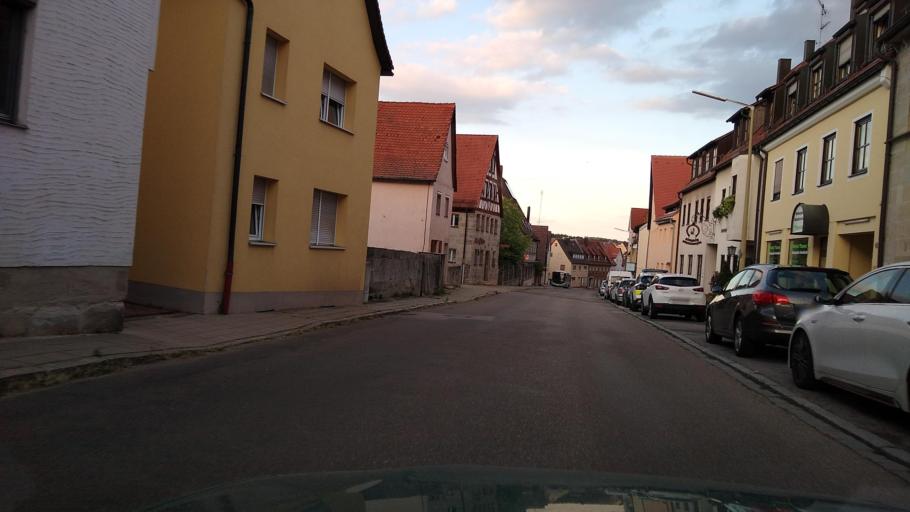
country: DE
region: Bavaria
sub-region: Regierungsbezirk Mittelfranken
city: Altdorf
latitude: 49.3871
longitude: 11.3554
